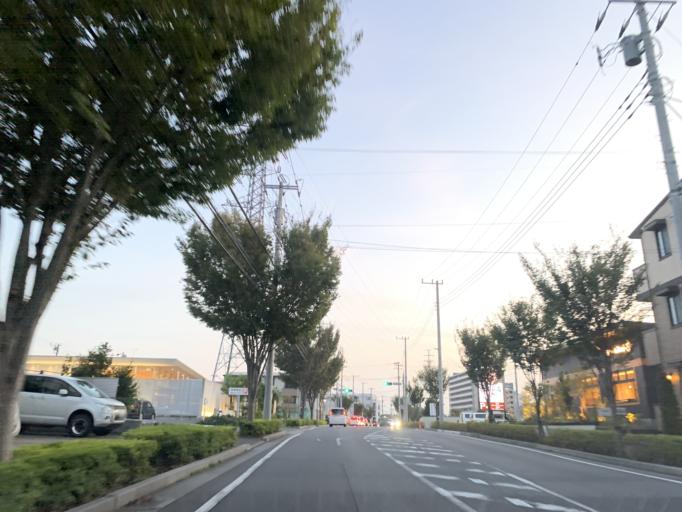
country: JP
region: Chiba
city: Nagareyama
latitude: 35.8749
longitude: 139.9324
